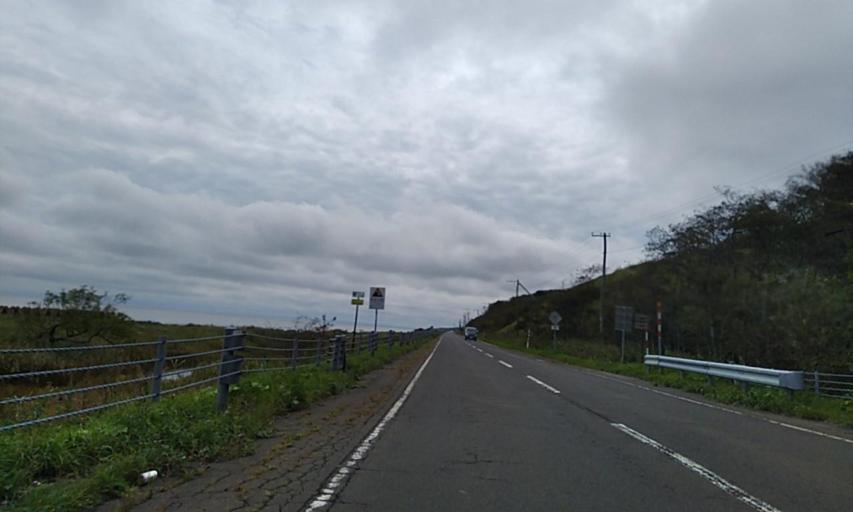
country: JP
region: Hokkaido
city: Shibetsu
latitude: 43.5070
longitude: 145.2450
